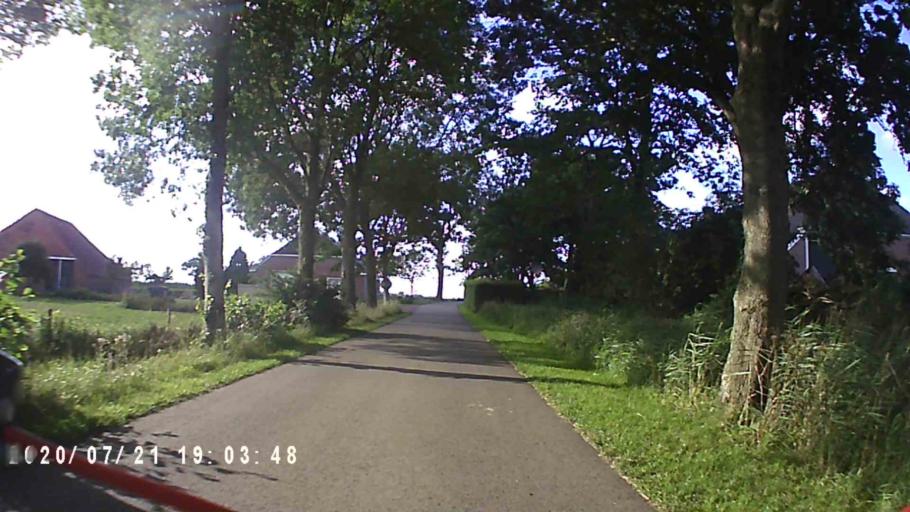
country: NL
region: Groningen
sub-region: Gemeente Slochteren
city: Slochteren
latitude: 53.2340
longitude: 6.7390
